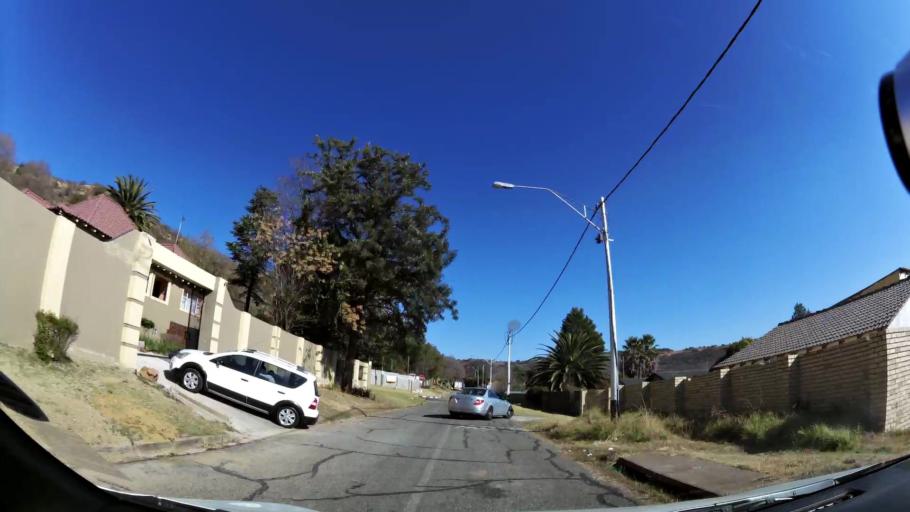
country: ZA
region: Gauteng
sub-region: City of Johannesburg Metropolitan Municipality
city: Johannesburg
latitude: -26.2791
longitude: 28.0112
